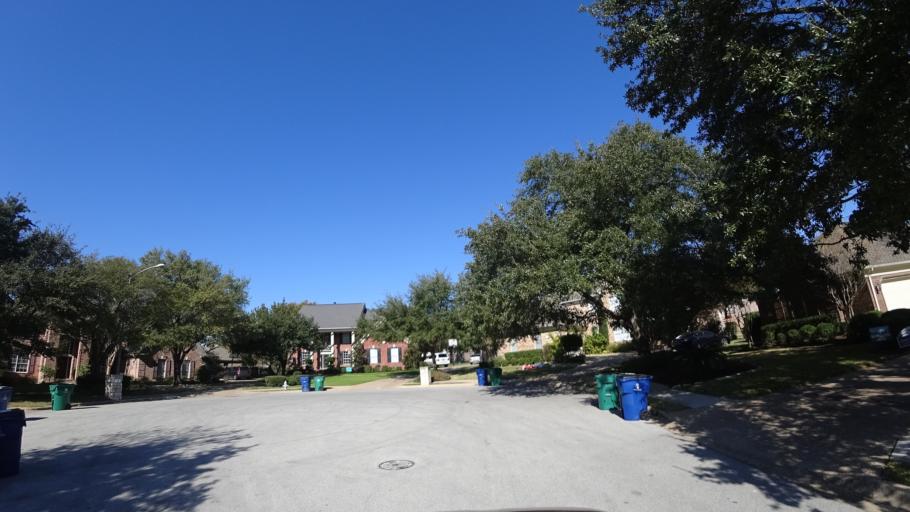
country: US
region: Texas
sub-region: Travis County
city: Lost Creek
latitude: 30.3743
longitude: -97.8490
